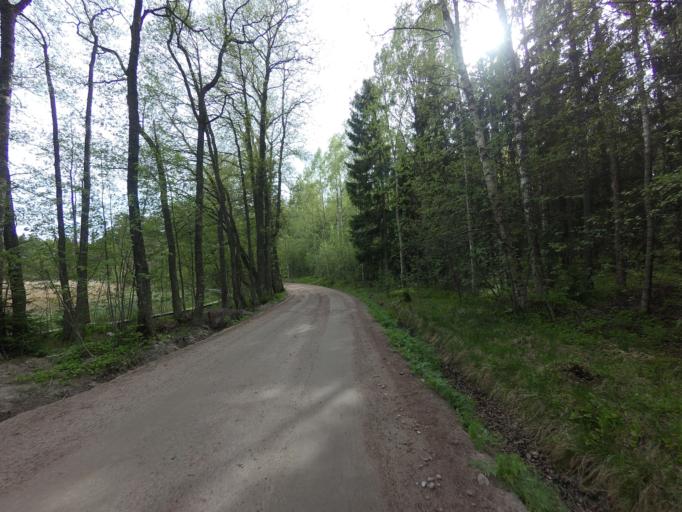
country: FI
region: Uusimaa
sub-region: Helsinki
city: Koukkuniemi
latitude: 60.1341
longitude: 24.6961
